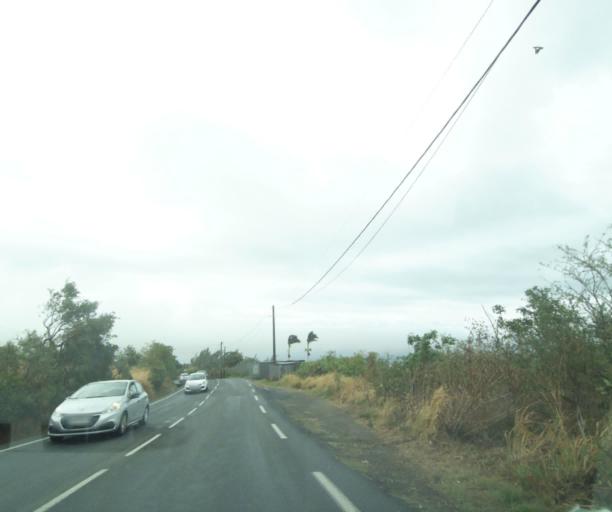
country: RE
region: Reunion
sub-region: Reunion
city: Saint-Paul
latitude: -21.0341
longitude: 55.2765
